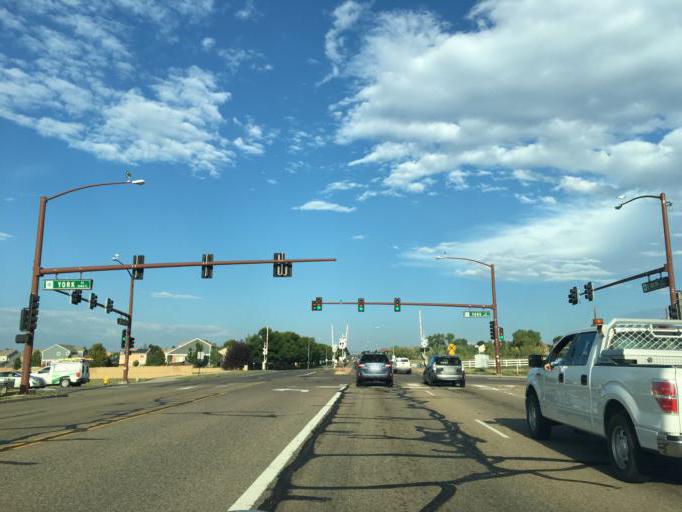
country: US
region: Colorado
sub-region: Adams County
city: Northglenn
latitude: 39.9428
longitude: -104.9601
